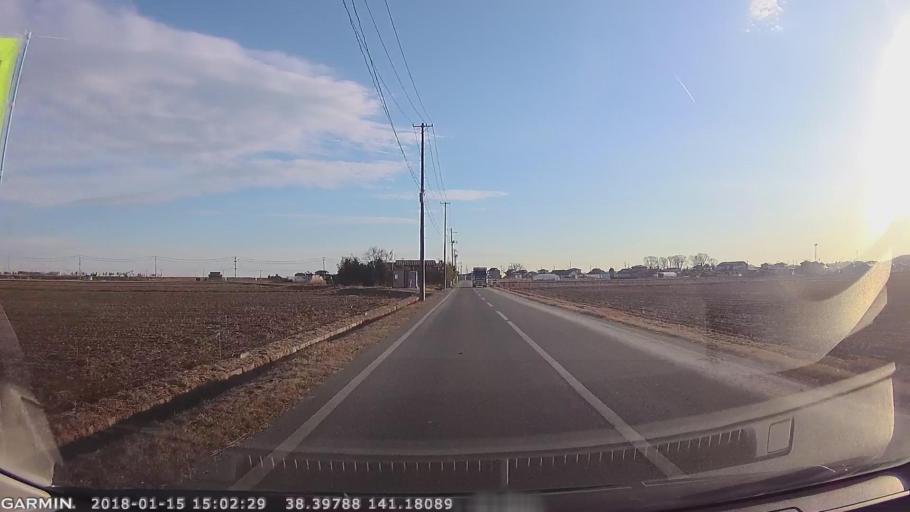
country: JP
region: Miyagi
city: Yamoto
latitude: 38.3979
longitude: 141.1809
